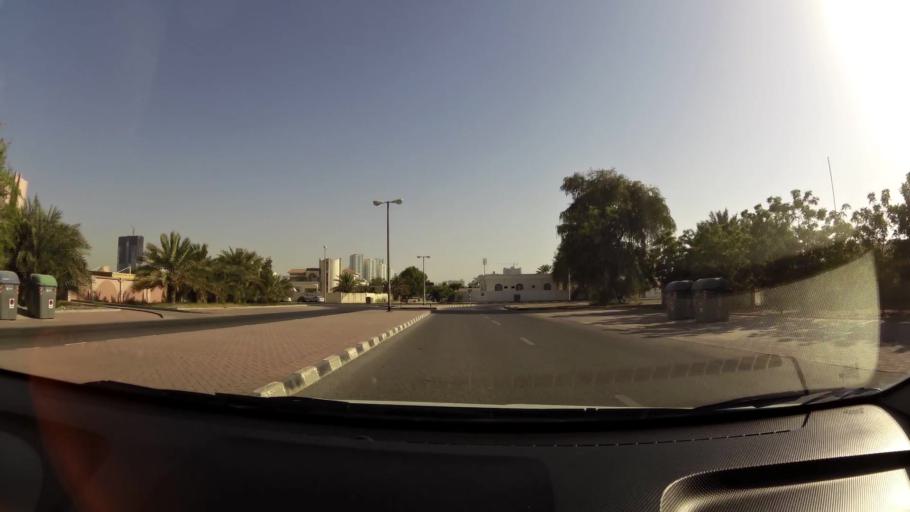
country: AE
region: Ajman
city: Ajman
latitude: 25.4038
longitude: 55.4713
